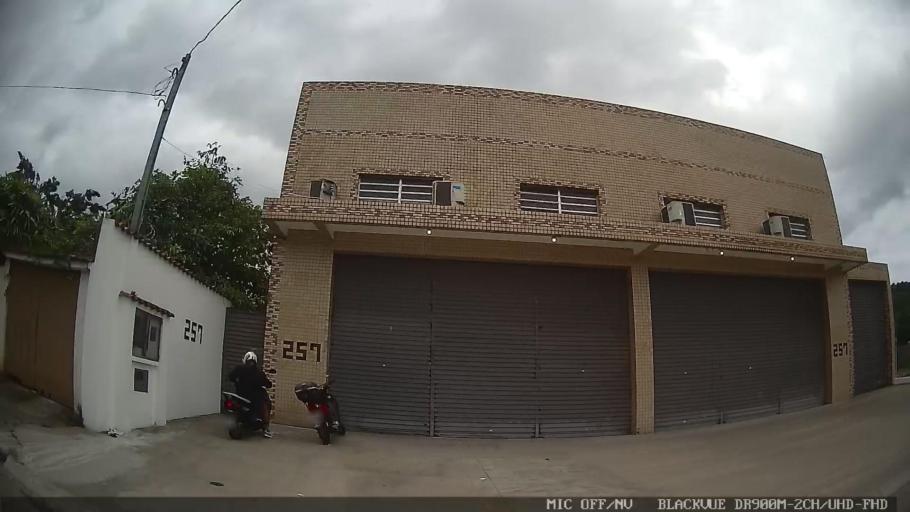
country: BR
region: Sao Paulo
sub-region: Guaruja
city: Guaruja
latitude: -23.9941
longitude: -46.2745
